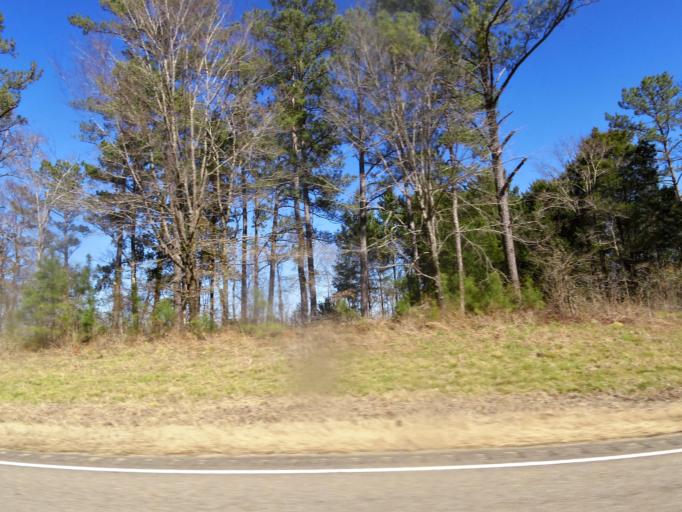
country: US
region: Alabama
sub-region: Montgomery County
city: Pike Road
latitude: 32.1781
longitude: -86.0812
